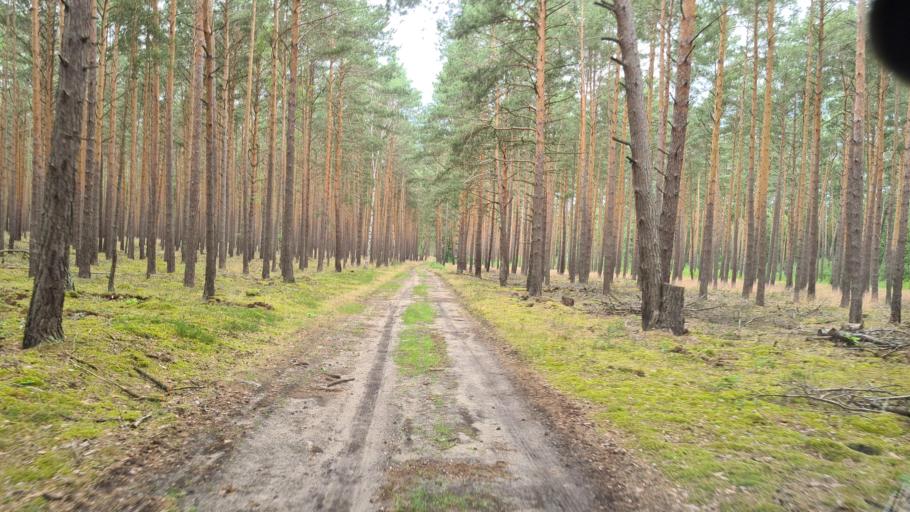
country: DE
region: Brandenburg
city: Bronkow
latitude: 51.7127
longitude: 13.8540
